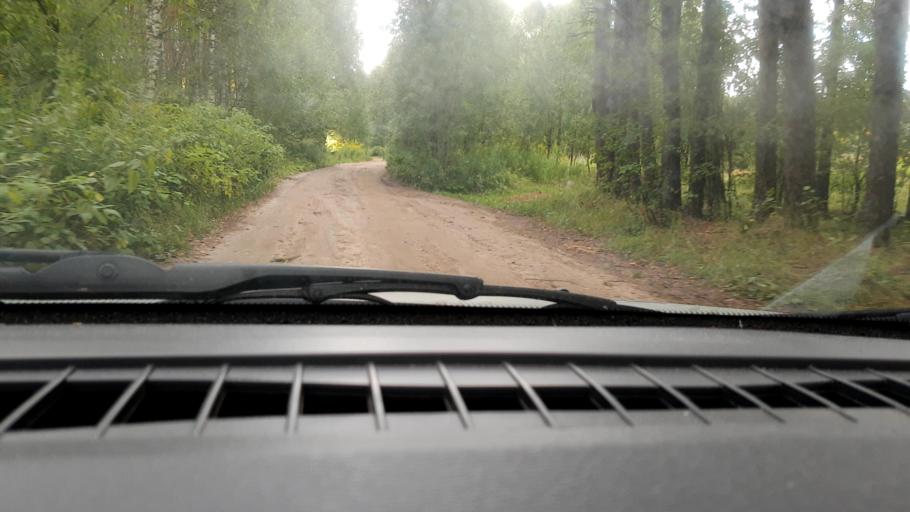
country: RU
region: Nizjnij Novgorod
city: Sitniki
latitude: 56.4510
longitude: 44.0208
